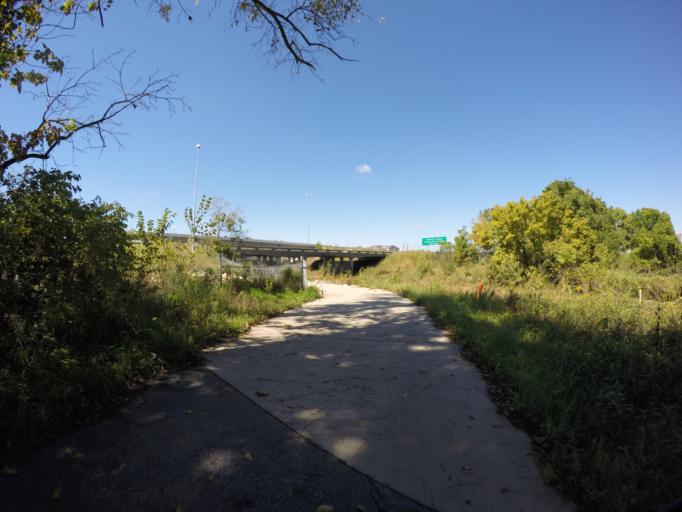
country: US
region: Kansas
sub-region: Johnson County
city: Lenexa
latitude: 38.9202
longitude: -94.7030
